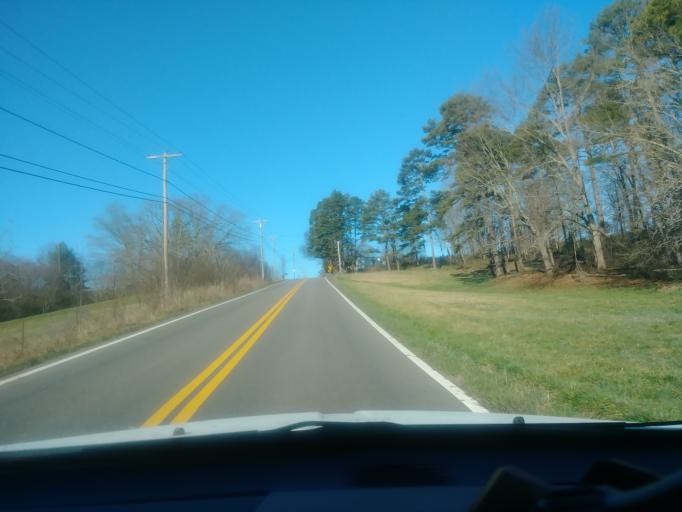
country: US
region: Tennessee
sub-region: Greene County
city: Mosheim
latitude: 36.1151
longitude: -82.9552
